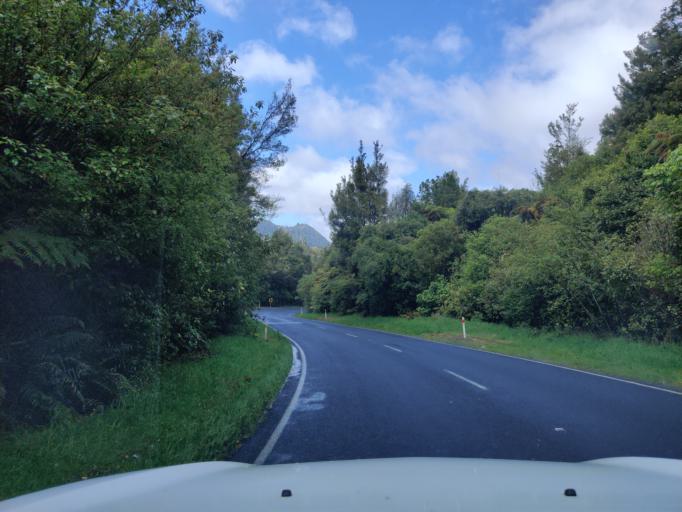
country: NZ
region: Bay of Plenty
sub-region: Rotorua District
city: Rotorua
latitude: -38.1822
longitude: 176.3271
